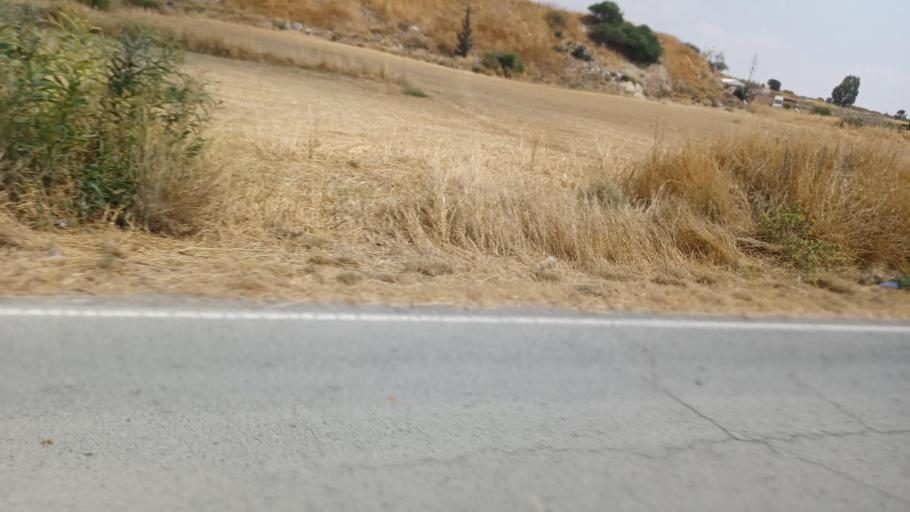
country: CY
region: Larnaka
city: Aradippou
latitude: 34.9459
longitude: 33.5621
